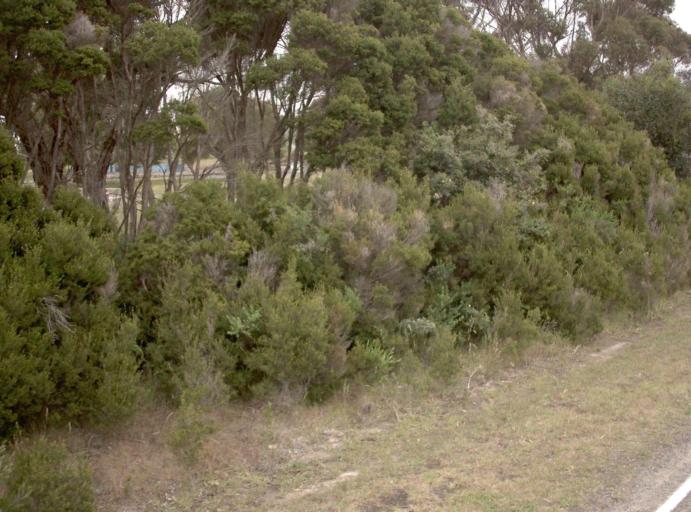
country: AU
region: Victoria
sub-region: Bass Coast
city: North Wonthaggi
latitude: -38.5996
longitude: 145.6042
